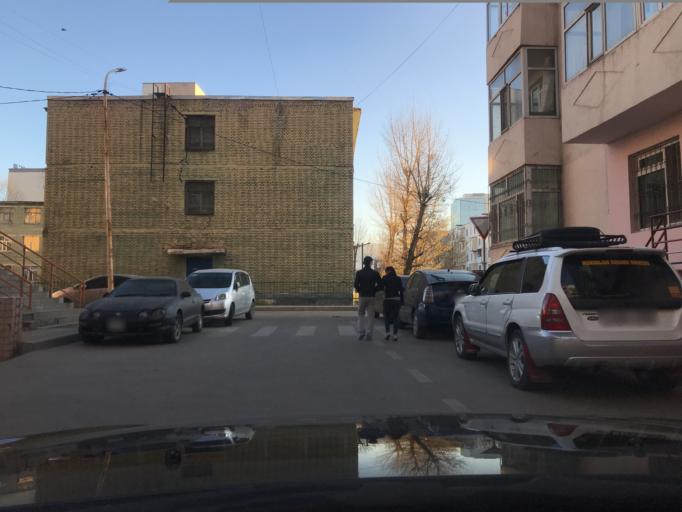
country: MN
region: Ulaanbaatar
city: Ulaanbaatar
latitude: 47.9271
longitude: 106.9058
